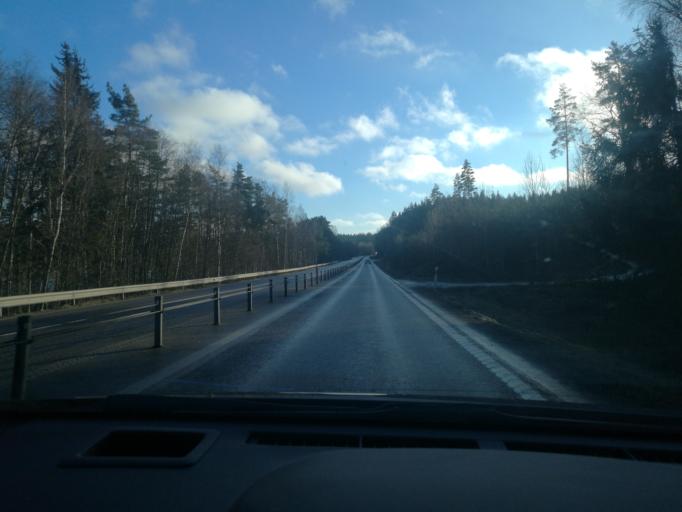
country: SE
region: OEstergoetland
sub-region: Norrkopings Kommun
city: Jursla
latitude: 58.7575
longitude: 16.1743
